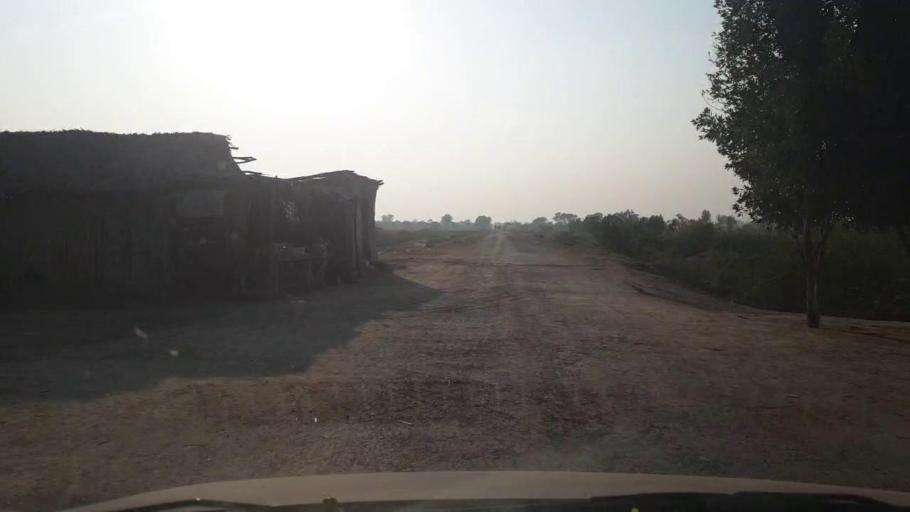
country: PK
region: Sindh
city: Mirwah Gorchani
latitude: 25.3660
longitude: 69.1541
